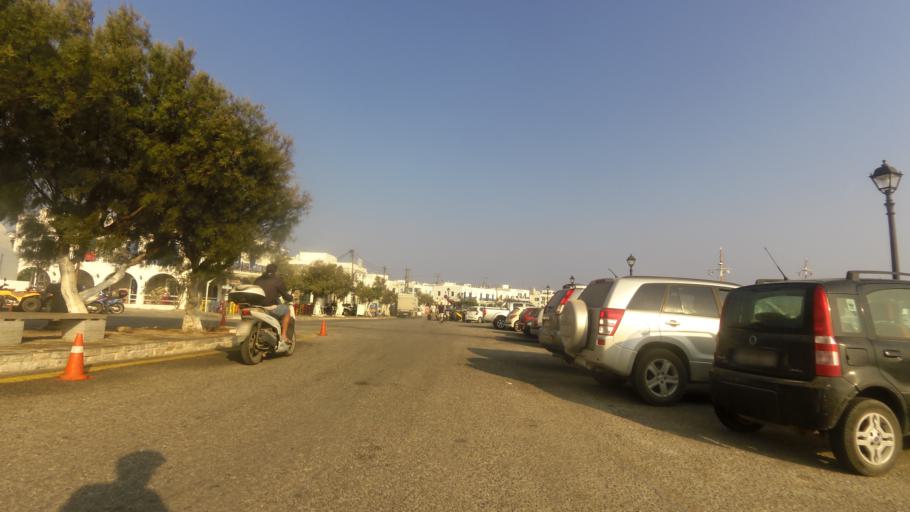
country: GR
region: South Aegean
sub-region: Nomos Kykladon
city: Antiparos
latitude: 37.0396
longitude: 25.0851
